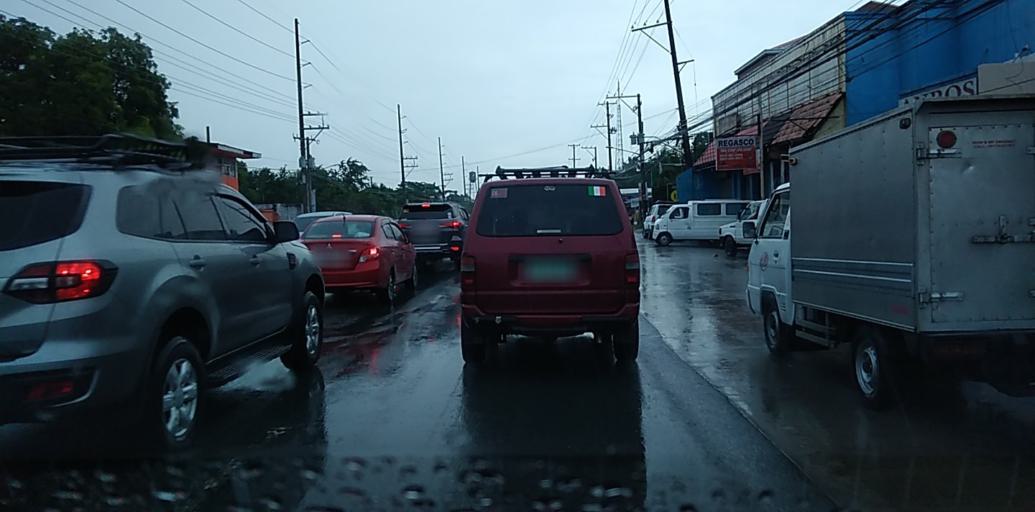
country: PH
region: Central Luzon
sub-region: Province of Pampanga
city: Bulaon
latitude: 15.0723
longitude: 120.6454
